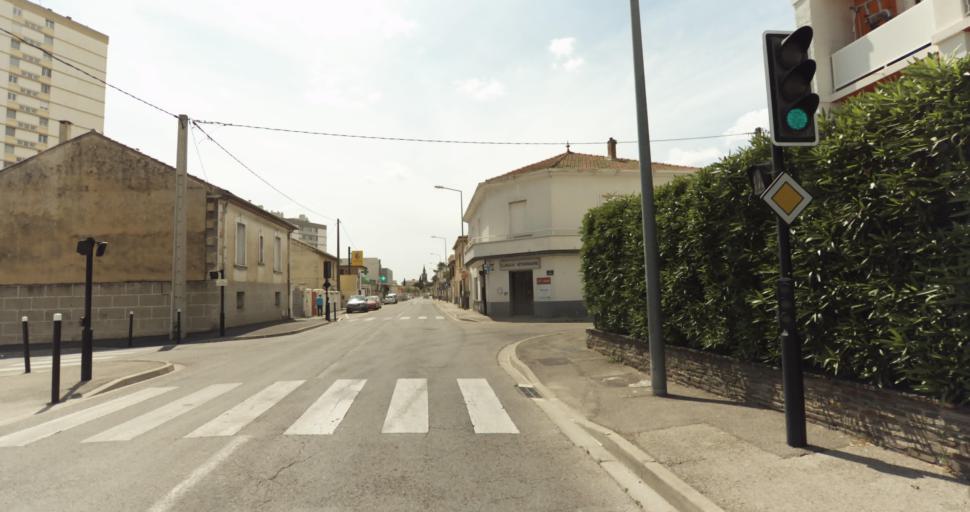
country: FR
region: Languedoc-Roussillon
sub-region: Departement du Gard
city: Nimes
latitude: 43.8444
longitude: 4.3830
